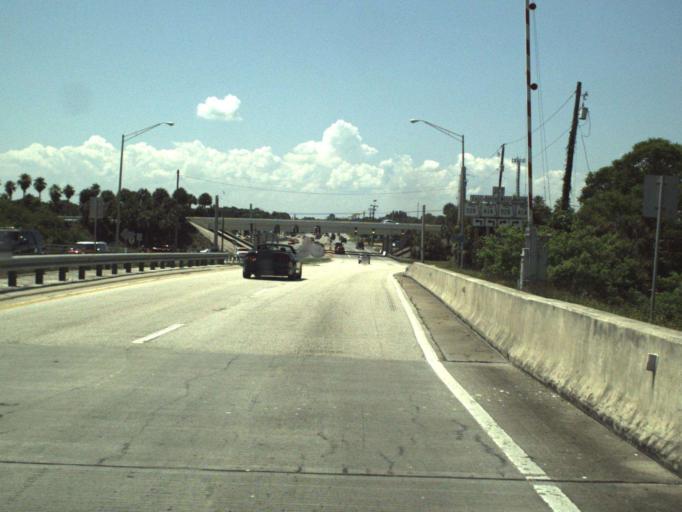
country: US
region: Florida
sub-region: Brevard County
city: Cocoa
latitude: 28.4074
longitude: -80.7060
